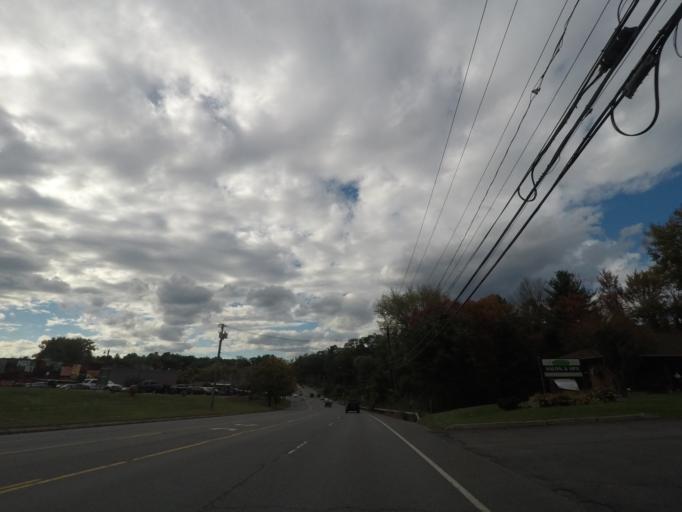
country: US
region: New York
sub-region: Albany County
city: Westmere
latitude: 42.6987
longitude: -73.8919
